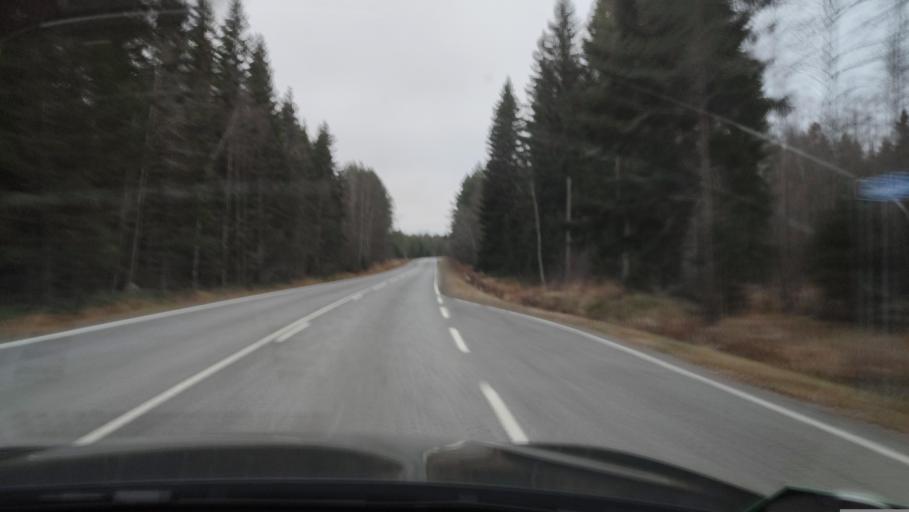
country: FI
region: Southern Ostrobothnia
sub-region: Suupohja
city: Karijoki
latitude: 62.3232
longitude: 21.8849
